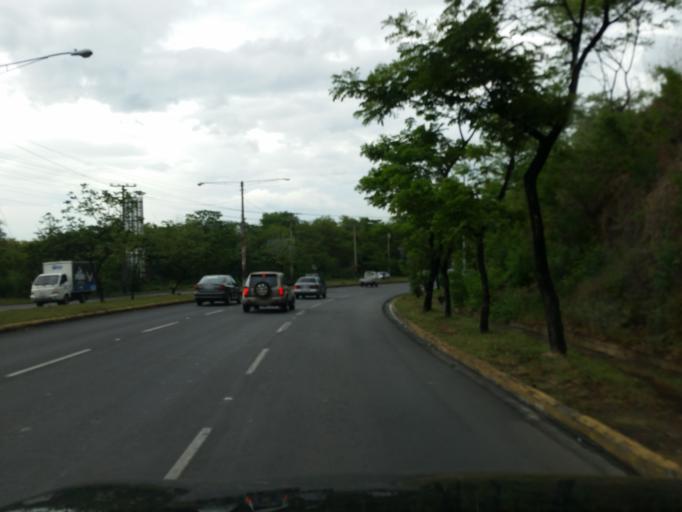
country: NI
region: Managua
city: Managua
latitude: 12.1116
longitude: -86.2757
